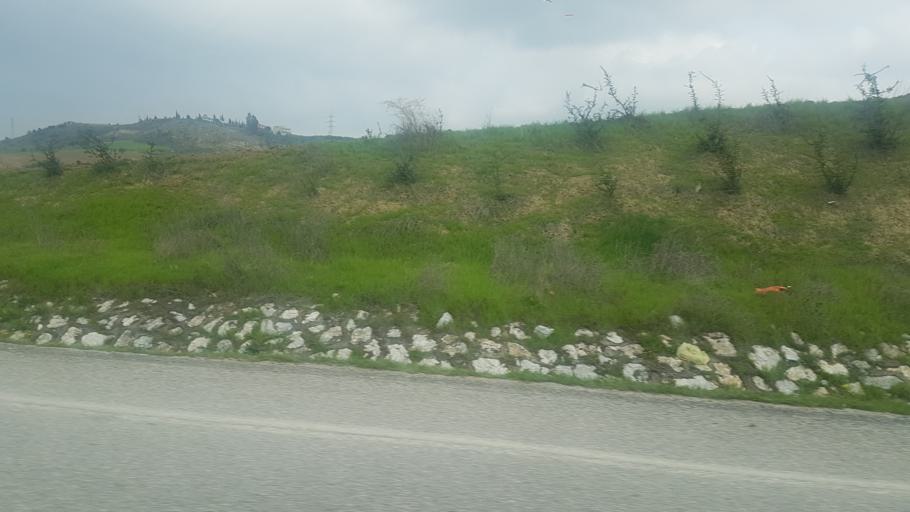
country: TR
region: Mersin
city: Yenice
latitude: 37.0573
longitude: 35.1684
